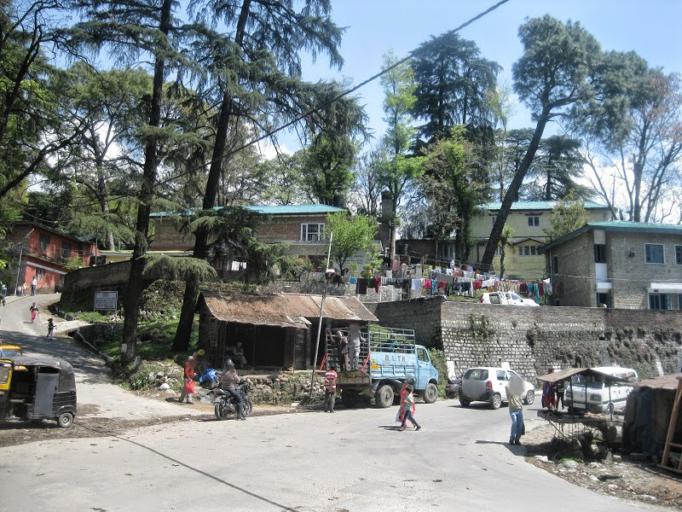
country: IN
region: Himachal Pradesh
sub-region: Kangra
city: Palampur
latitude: 32.1126
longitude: 76.5355
